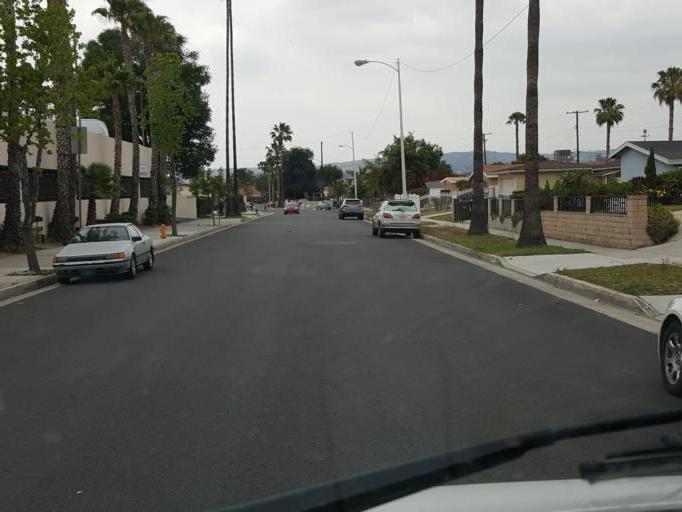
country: US
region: California
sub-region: Los Angeles County
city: Rowland Heights
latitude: 33.9892
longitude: -117.9038
